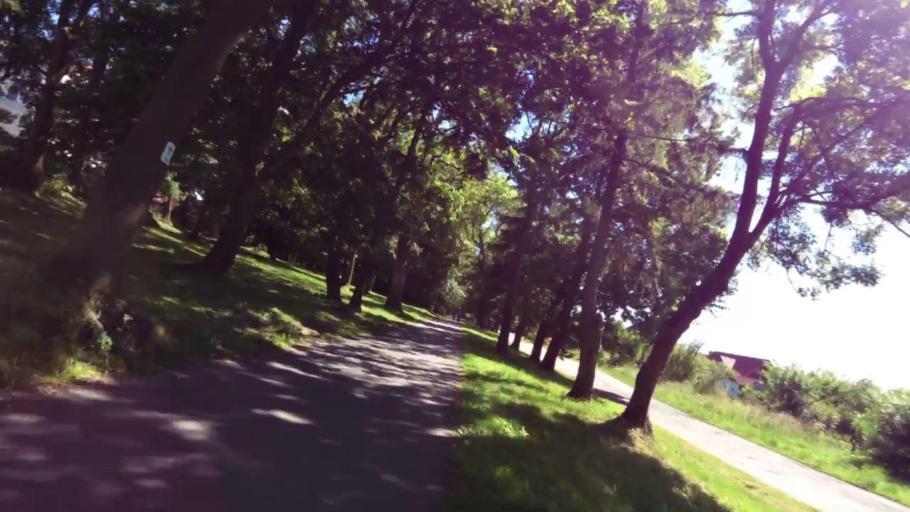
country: PL
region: West Pomeranian Voivodeship
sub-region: Powiat bialogardzki
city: Karlino
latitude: 54.0423
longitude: 15.8804
